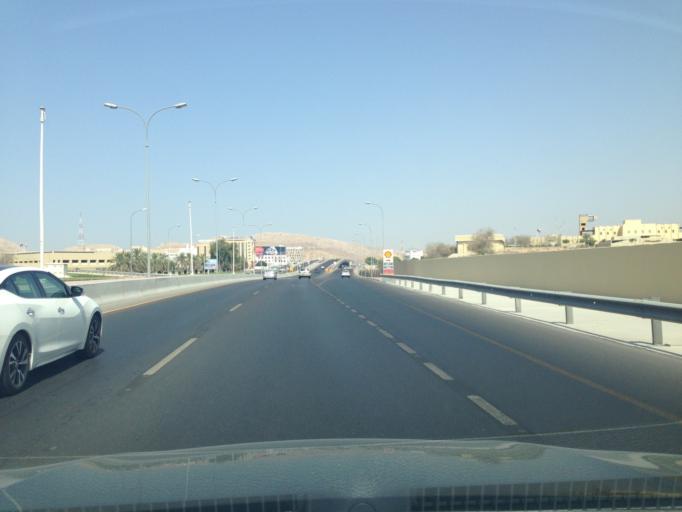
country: OM
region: Muhafazat Masqat
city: Bawshar
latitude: 23.6137
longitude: 58.4866
